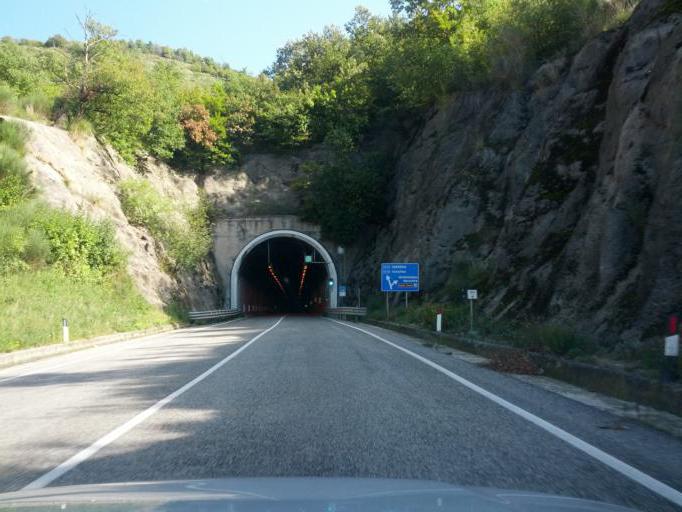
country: IT
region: Campania
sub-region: Provincia di Caserta
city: Mignano Monte Lungo
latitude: 41.4413
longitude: 14.0019
